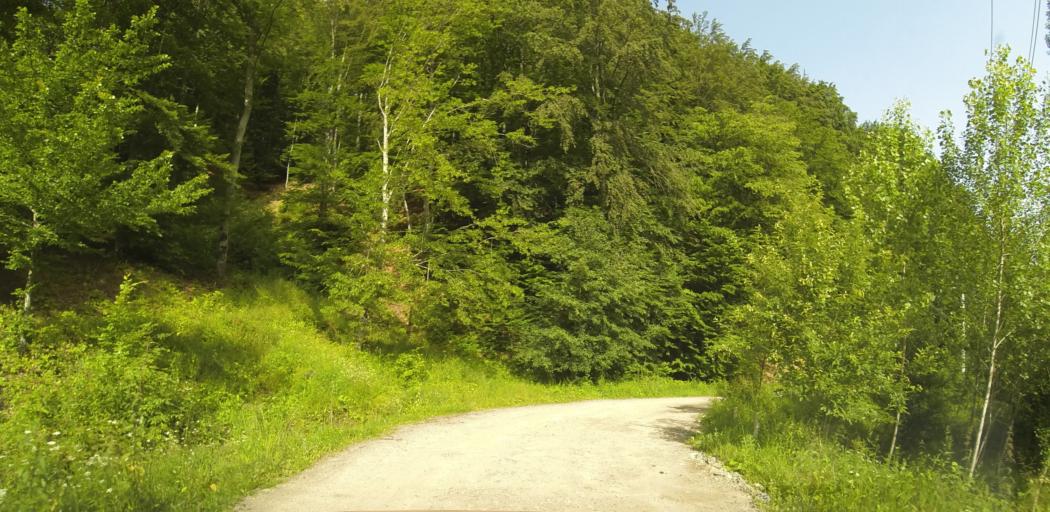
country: RO
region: Valcea
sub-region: Oras Baile Olanesti
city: Baile Olanesti
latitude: 45.2189
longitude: 24.2162
